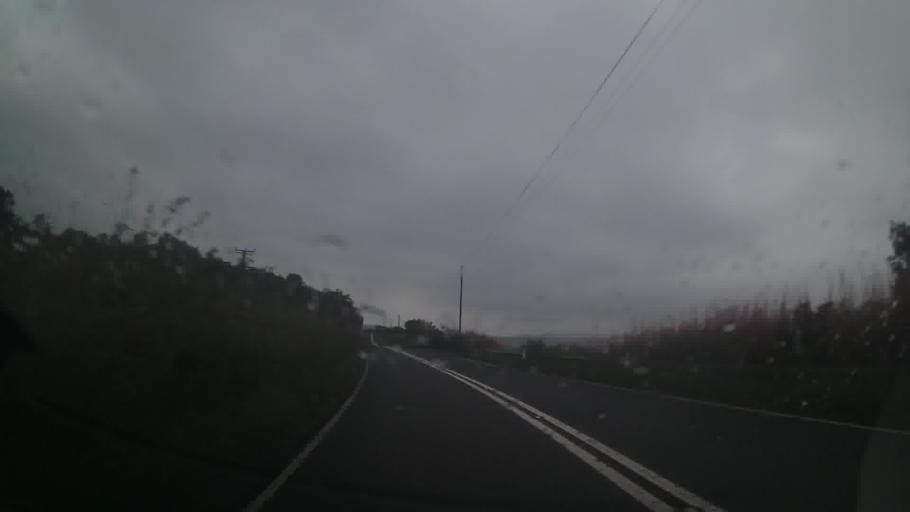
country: GB
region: Scotland
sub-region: North Ayrshire
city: Skelmorlie
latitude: 55.8416
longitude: -4.8911
